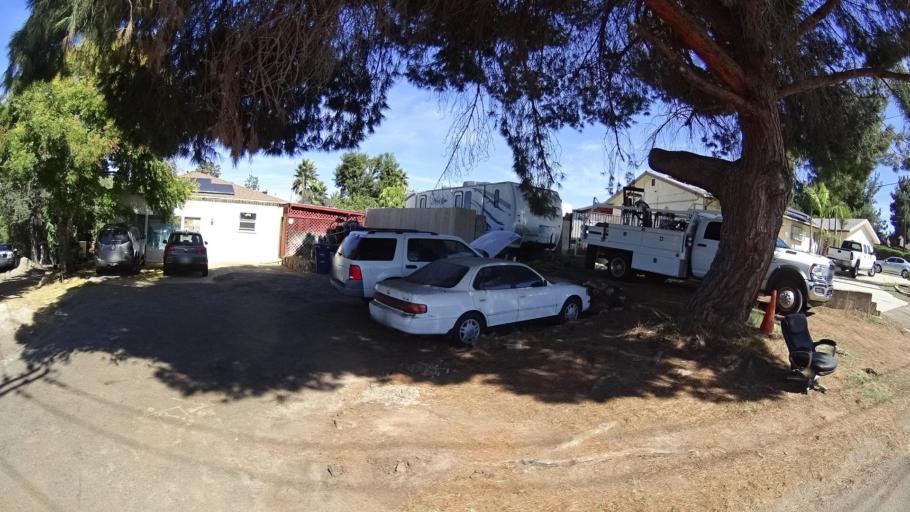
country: US
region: California
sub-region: San Diego County
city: Casa de Oro-Mount Helix
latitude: 32.7465
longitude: -116.9754
